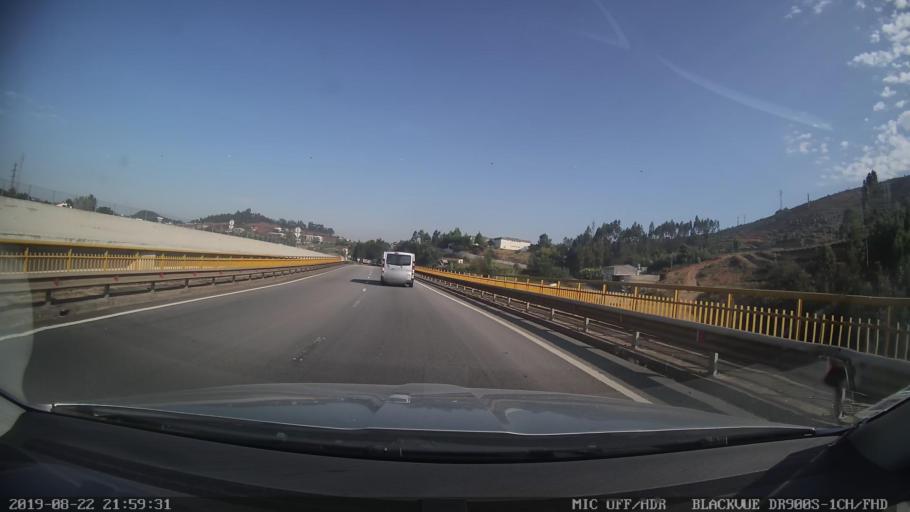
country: PT
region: Coimbra
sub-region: Coimbra
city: Coimbra
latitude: 40.1804
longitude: -8.3920
